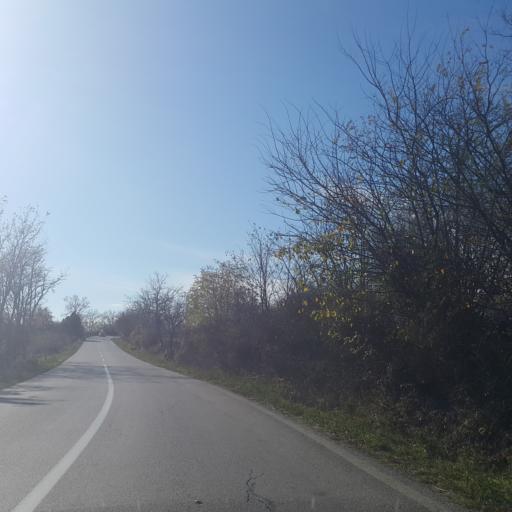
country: RS
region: Central Serbia
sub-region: Sumadijski Okrug
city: Topola
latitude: 44.2515
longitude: 20.7863
